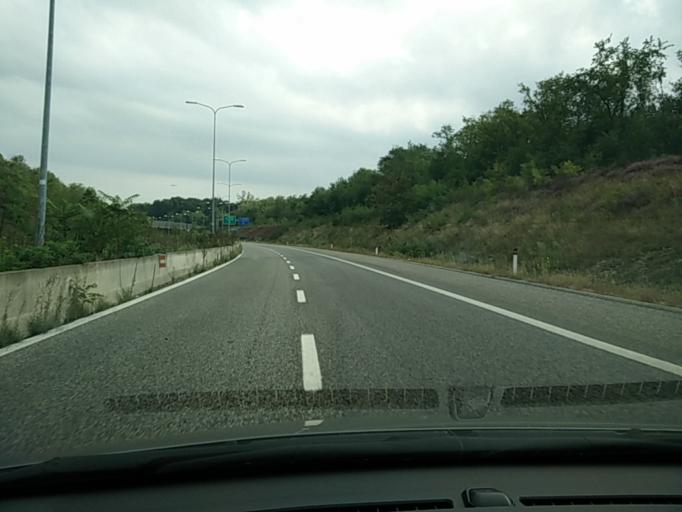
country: IT
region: Lombardy
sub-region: Provincia di Varese
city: Lonate Pozzolo
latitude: 45.5884
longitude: 8.7161
